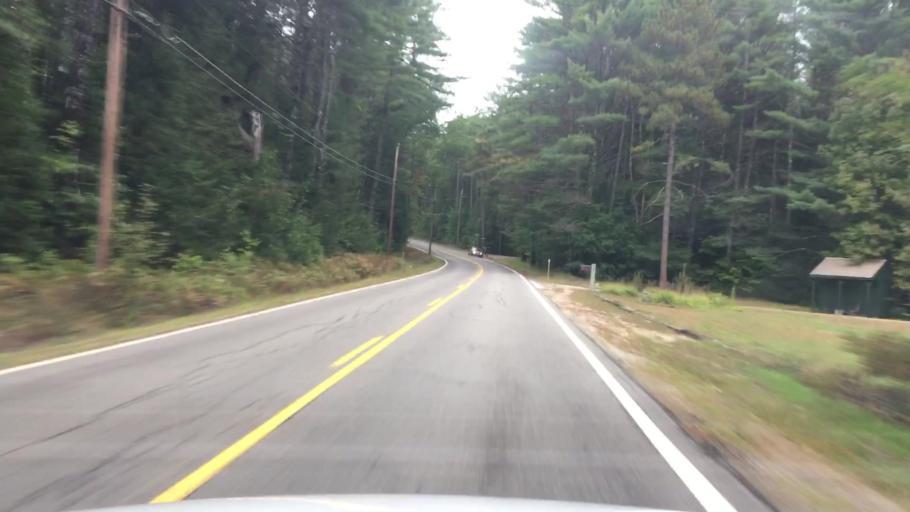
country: US
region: New Hampshire
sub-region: Carroll County
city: Effingham
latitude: 43.7544
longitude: -71.0013
